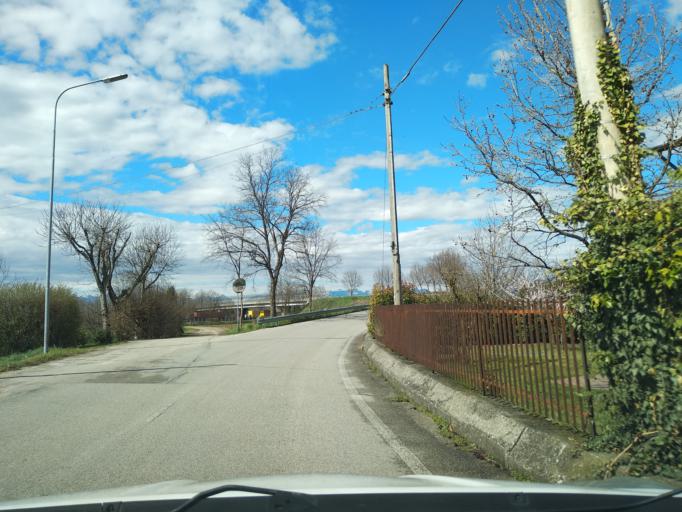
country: IT
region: Veneto
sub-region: Provincia di Vicenza
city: Vigardolo
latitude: 45.6102
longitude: 11.6028
